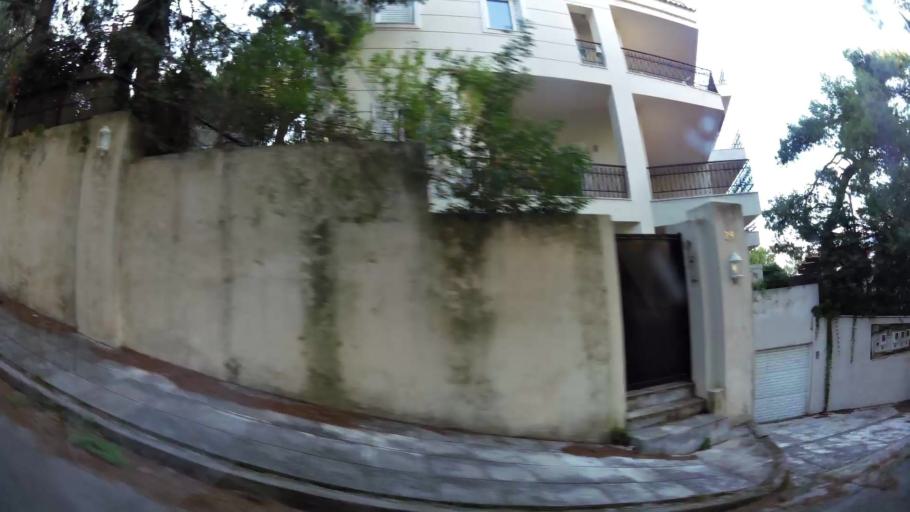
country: GR
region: Attica
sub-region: Nomarchia Athinas
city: Nea Erythraia
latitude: 38.0926
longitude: 23.8320
